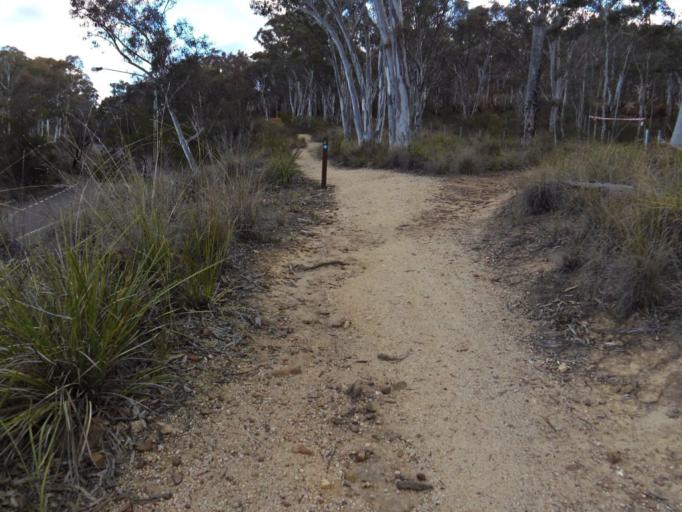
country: AU
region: Australian Capital Territory
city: Acton
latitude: -35.2656
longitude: 149.1099
